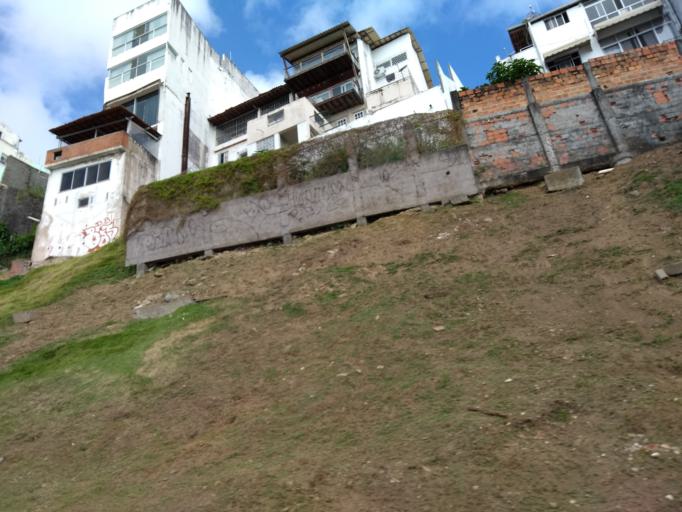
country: BR
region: Bahia
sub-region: Salvador
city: Salvador
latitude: -12.9842
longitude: -38.5209
